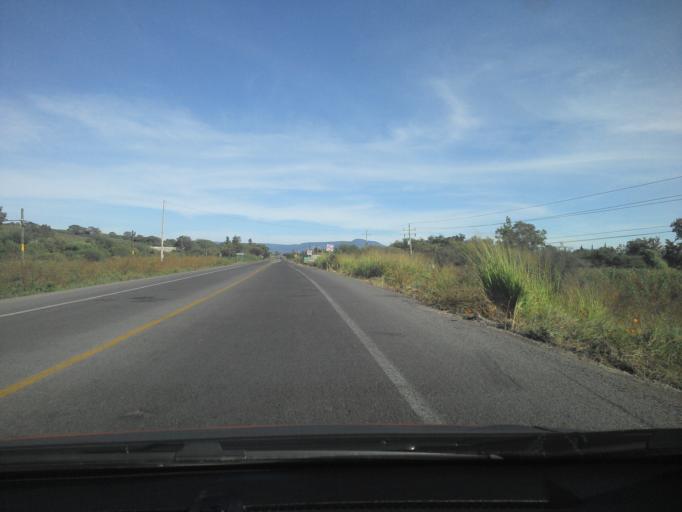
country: MX
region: Jalisco
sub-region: Teuchitlan
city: La Estanzuela
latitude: 20.6740
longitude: -103.8294
